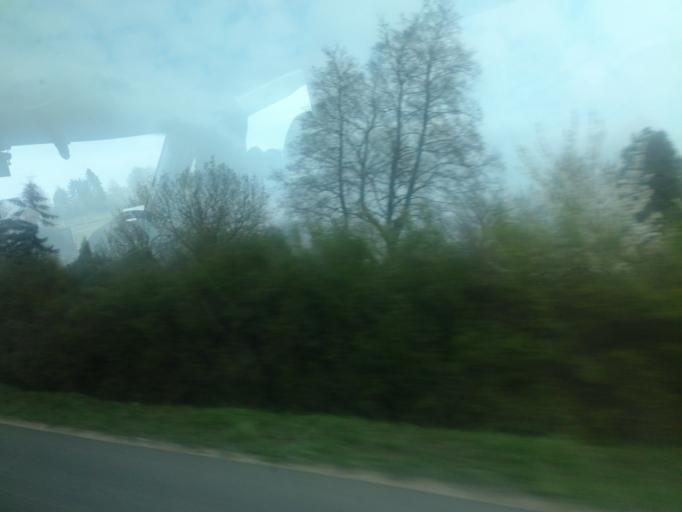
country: DE
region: North Rhine-Westphalia
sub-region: Regierungsbezirk Dusseldorf
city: Kamp-Lintfort
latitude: 51.5039
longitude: 6.5679
